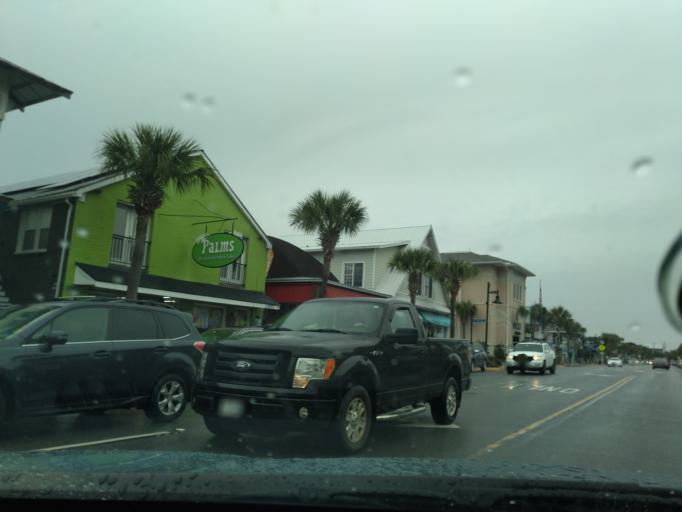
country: US
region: South Carolina
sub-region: Charleston County
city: Folly Beach
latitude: 32.6556
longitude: -79.9408
